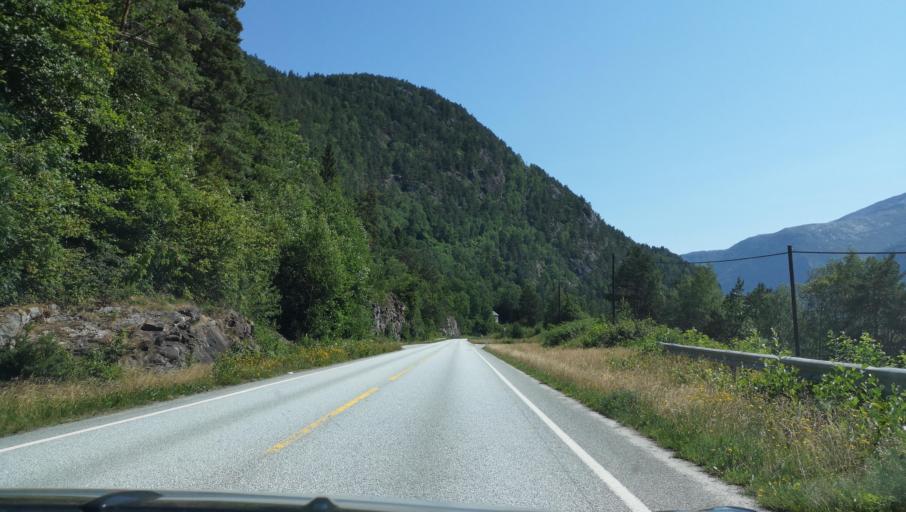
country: NO
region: Hordaland
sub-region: Ulvik
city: Ulvik
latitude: 60.4906
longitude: 6.8596
